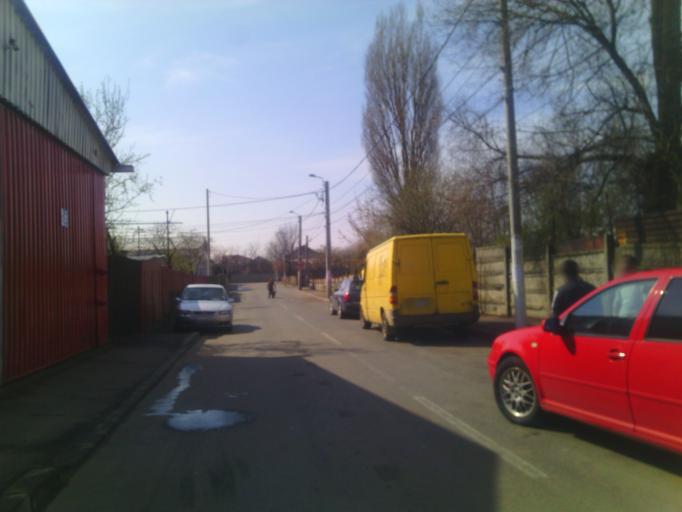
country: RO
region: Ilfov
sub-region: Comuna Jilava
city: Jilava
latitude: 44.3686
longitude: 26.1017
